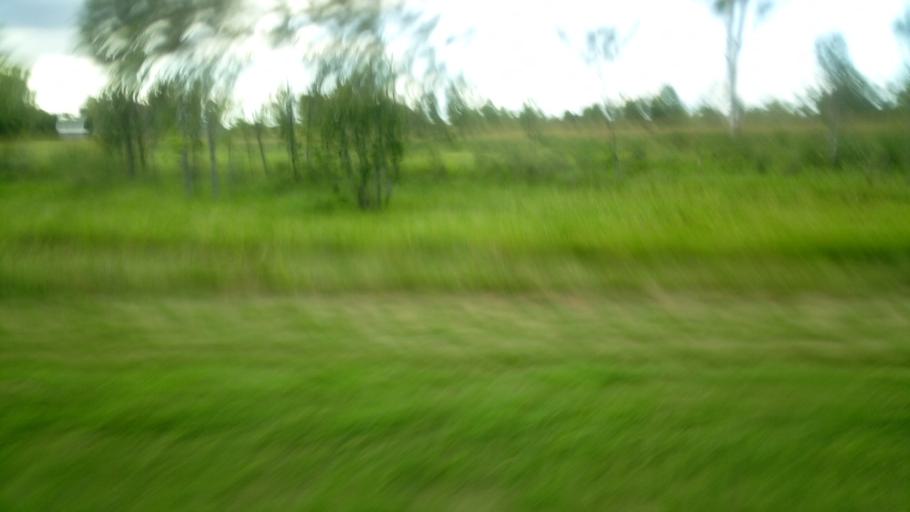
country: AU
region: Queensland
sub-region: Tablelands
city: Mareeba
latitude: -17.0046
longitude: 145.4501
